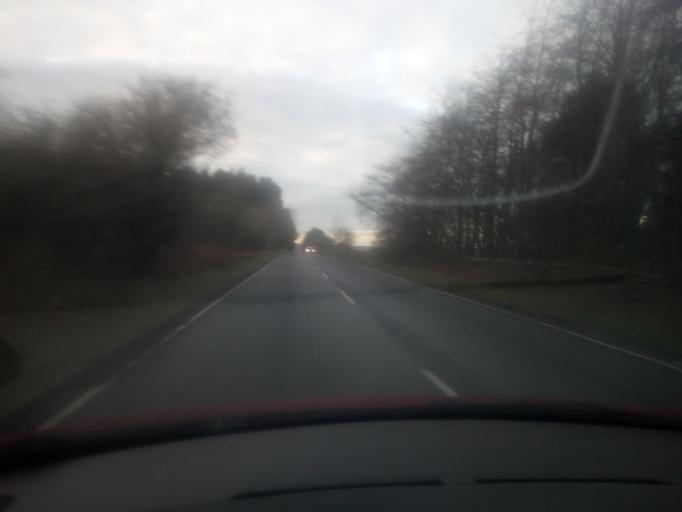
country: GB
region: England
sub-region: Northumberland
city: Healey
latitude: 54.9260
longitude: -1.9604
